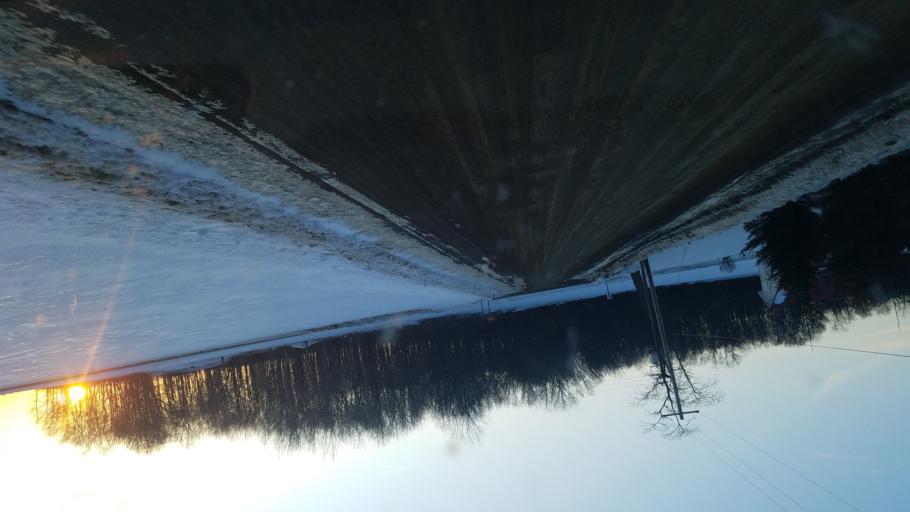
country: US
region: Pennsylvania
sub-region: Tioga County
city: Westfield
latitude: 42.0016
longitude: -77.6900
